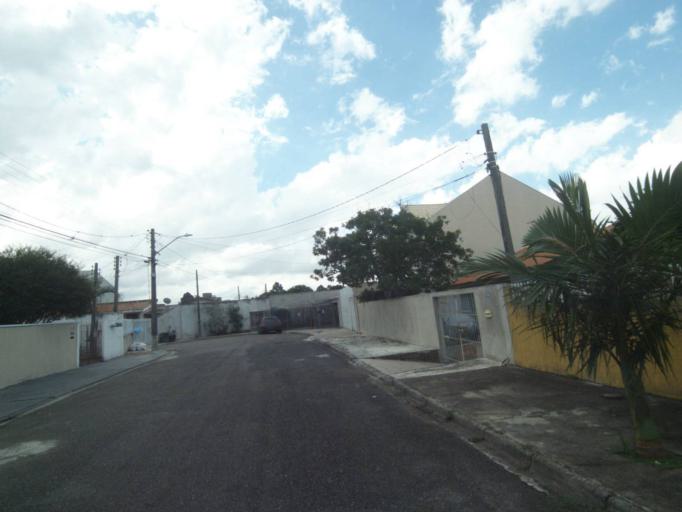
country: BR
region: Parana
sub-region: Pinhais
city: Pinhais
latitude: -25.4460
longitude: -49.2127
